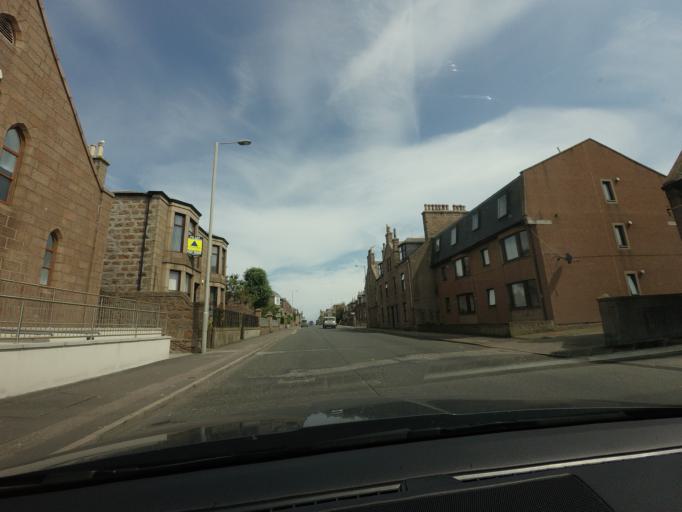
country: GB
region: Scotland
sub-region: Aberdeenshire
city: Peterhead
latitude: 57.5067
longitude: -1.7862
